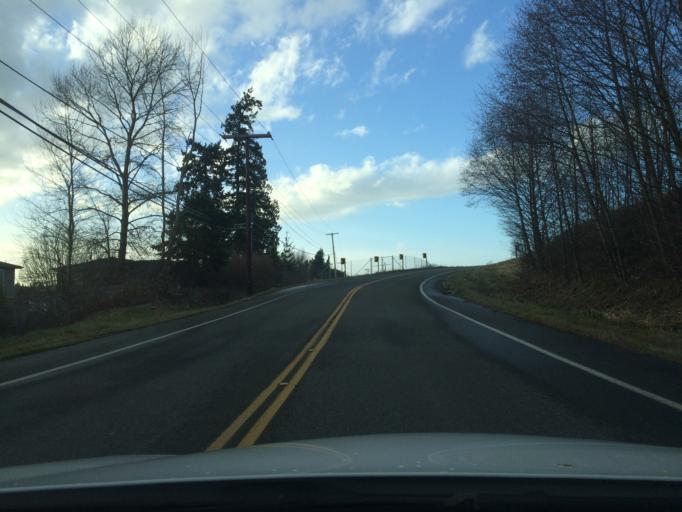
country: US
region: Washington
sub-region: Whatcom County
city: Birch Bay
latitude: 48.9435
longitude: -122.7775
